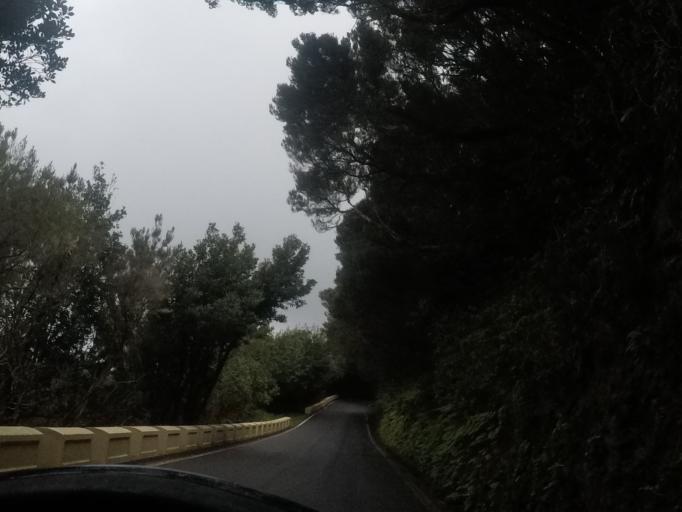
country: ES
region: Canary Islands
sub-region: Provincia de Santa Cruz de Tenerife
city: Santa Cruz de Tenerife
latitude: 28.5358
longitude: -16.2396
